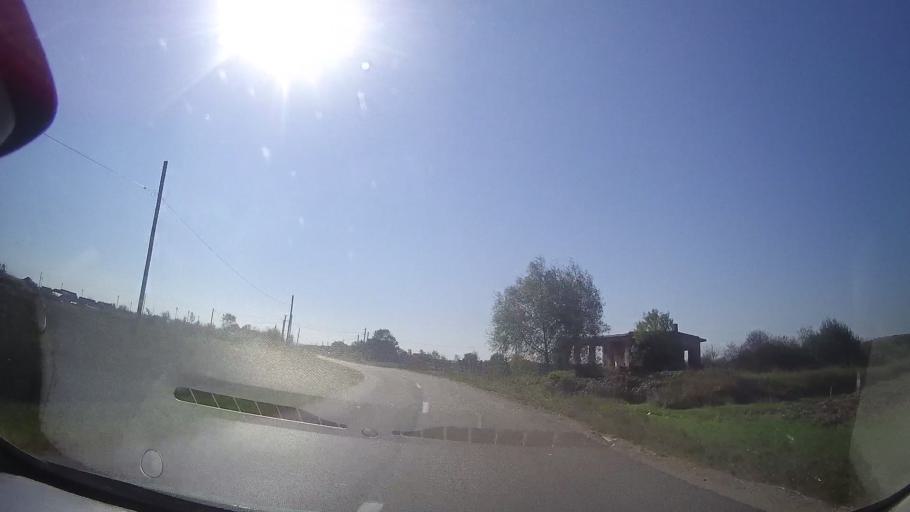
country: RO
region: Timis
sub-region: Comuna Bethausen
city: Bethausen
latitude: 45.8425
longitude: 21.9597
